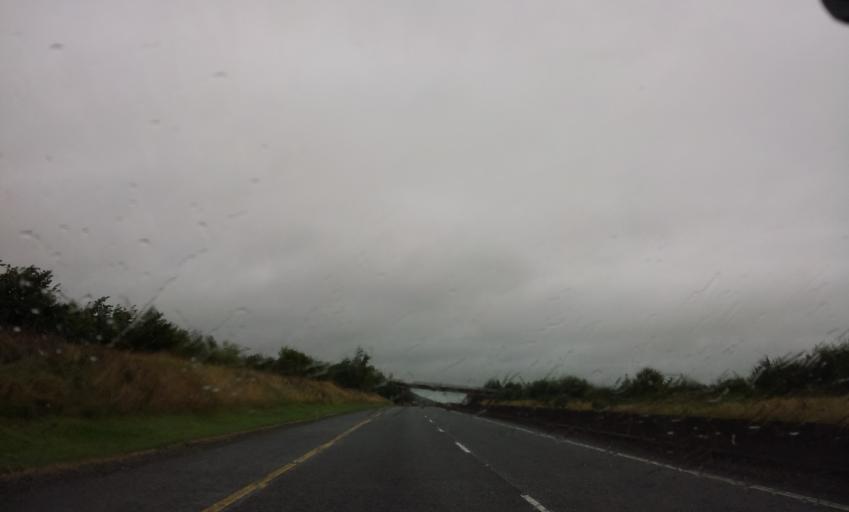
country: IE
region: Munster
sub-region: County Cork
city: Rathcormac
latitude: 52.0851
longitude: -8.2950
